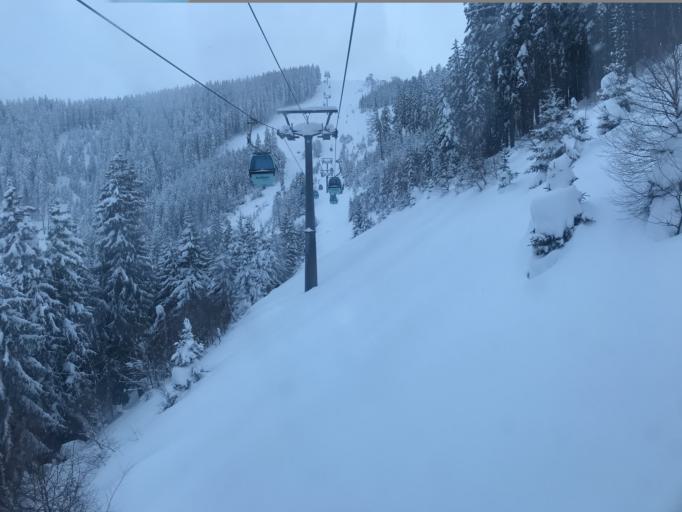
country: AT
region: Salzburg
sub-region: Politischer Bezirk Zell am See
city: Zell am See
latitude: 47.3116
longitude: 12.7580
